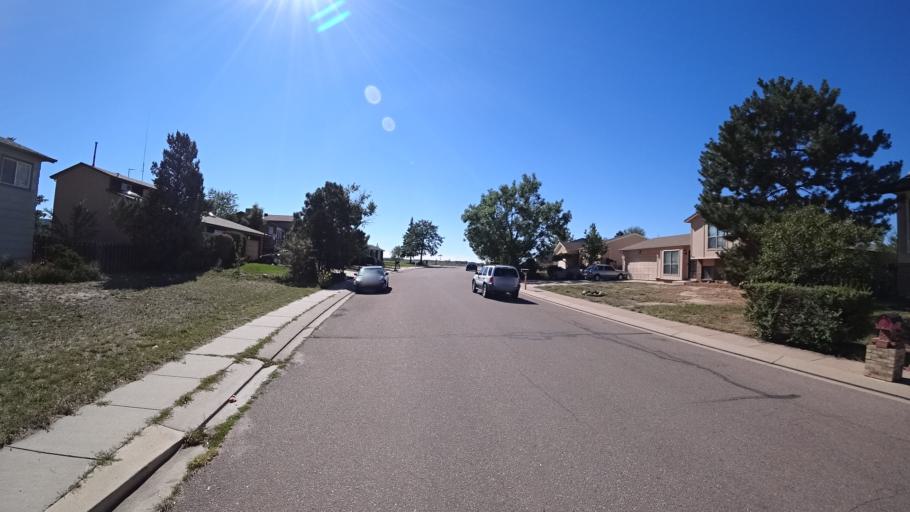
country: US
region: Colorado
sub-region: El Paso County
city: Cimarron Hills
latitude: 38.8182
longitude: -104.7318
